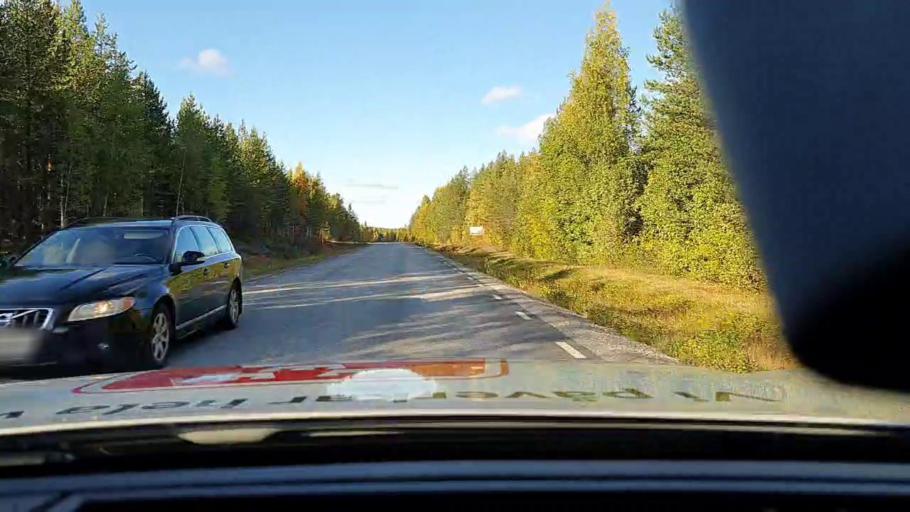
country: SE
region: Norrbotten
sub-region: Pitea Kommun
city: Norrfjarden
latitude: 65.4962
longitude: 21.4751
